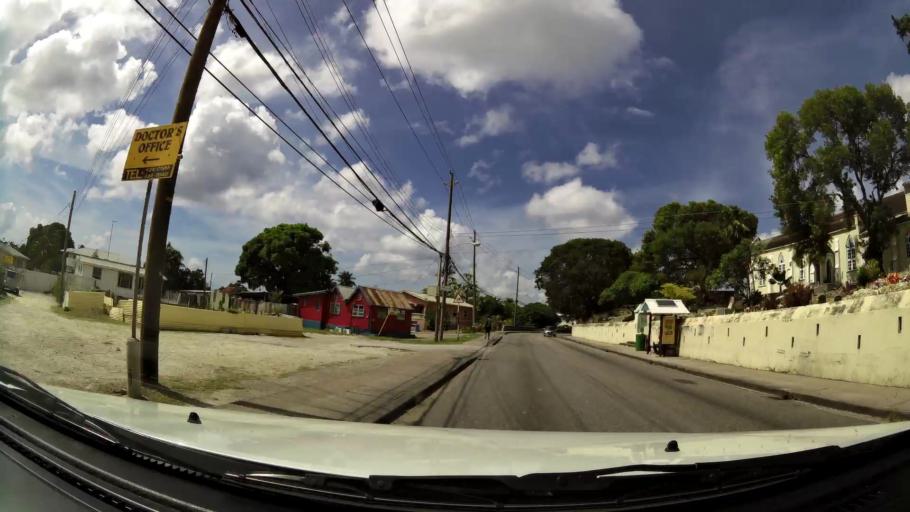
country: BB
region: Saint Michael
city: Bridgetown
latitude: 13.1256
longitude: -59.6257
